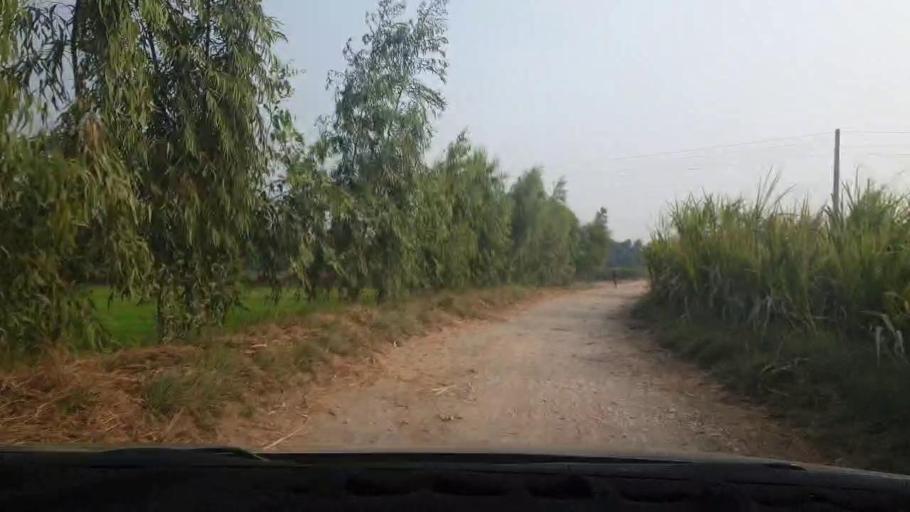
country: PK
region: Sindh
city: Matiari
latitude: 25.5820
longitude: 68.5167
